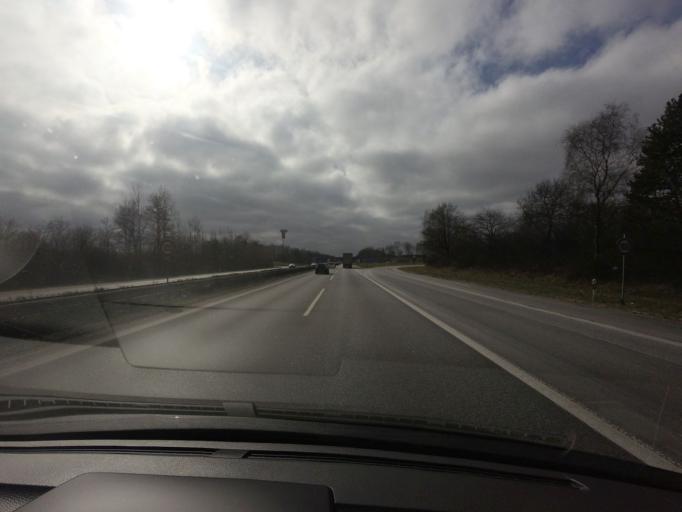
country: DE
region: Schleswig-Holstein
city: Nutzen
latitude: 53.8511
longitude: 9.9378
